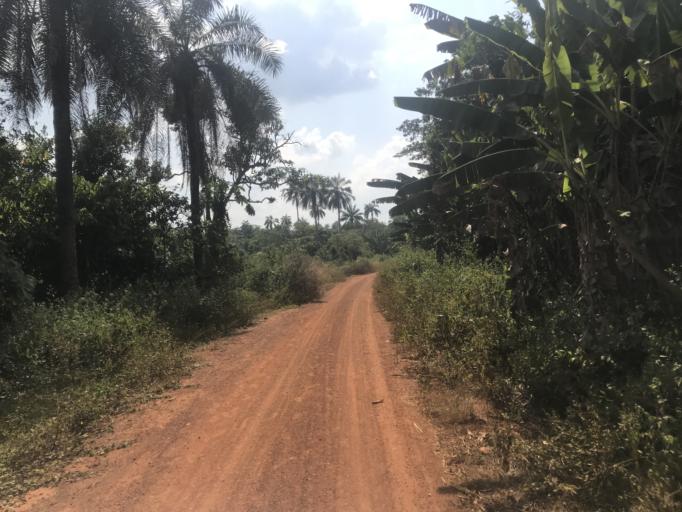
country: NG
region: Osun
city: Ibokun
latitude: 7.8198
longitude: 4.6992
